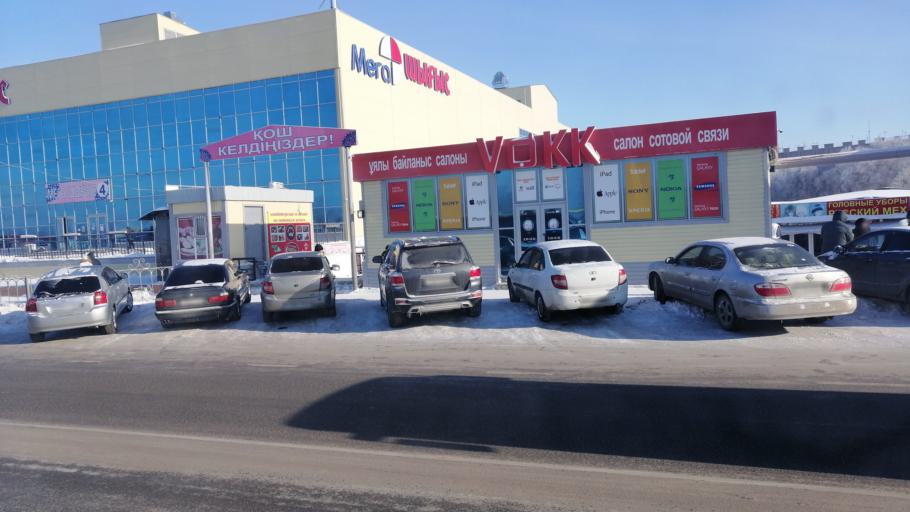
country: KZ
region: Aqtoebe
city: Aqtobe
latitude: 50.2962
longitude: 57.1976
